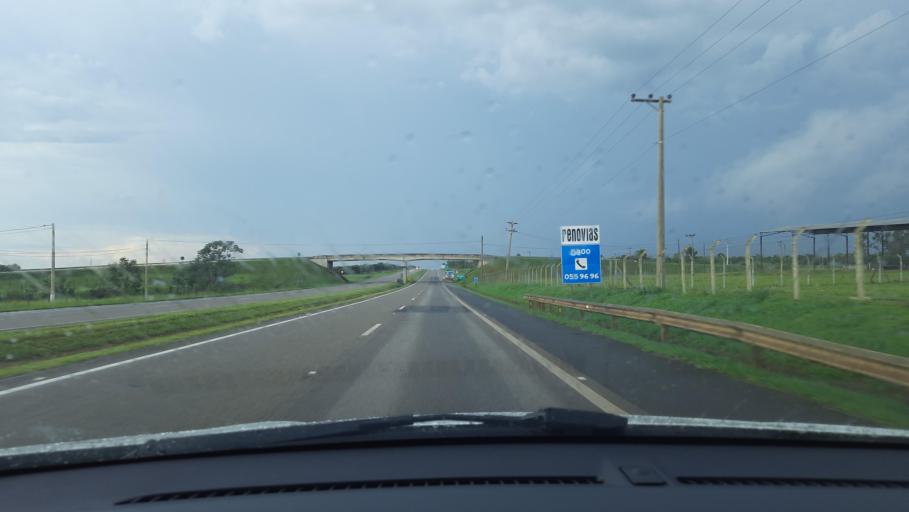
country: BR
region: Sao Paulo
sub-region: Casa Branca
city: Casa Branca
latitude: -21.7507
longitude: -47.0716
